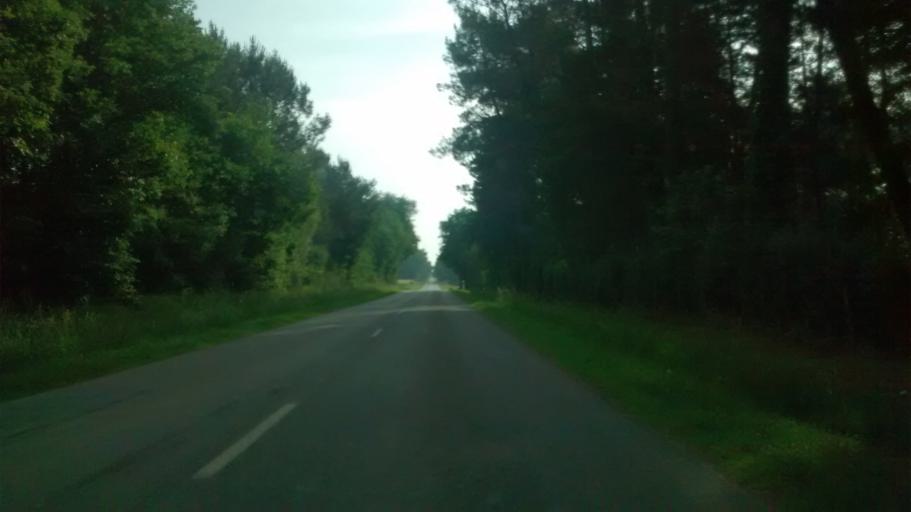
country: FR
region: Brittany
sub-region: Departement du Morbihan
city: Guer
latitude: 47.8772
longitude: -2.1985
